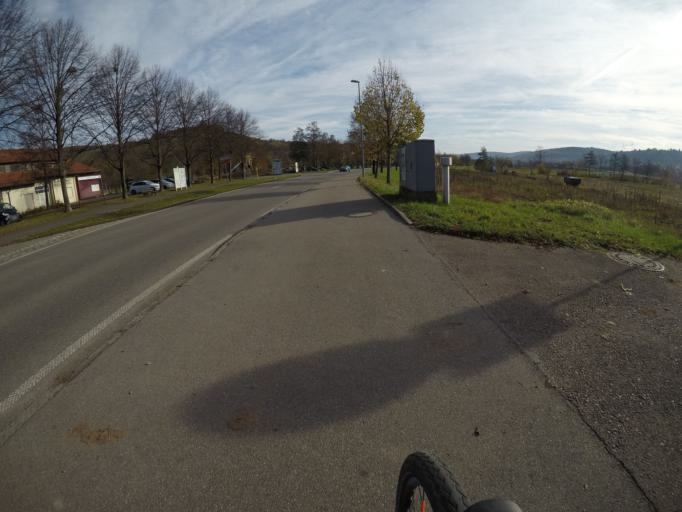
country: DE
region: Baden-Wuerttemberg
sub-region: Regierungsbezirk Stuttgart
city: Winterbach
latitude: 48.8149
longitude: 9.4269
